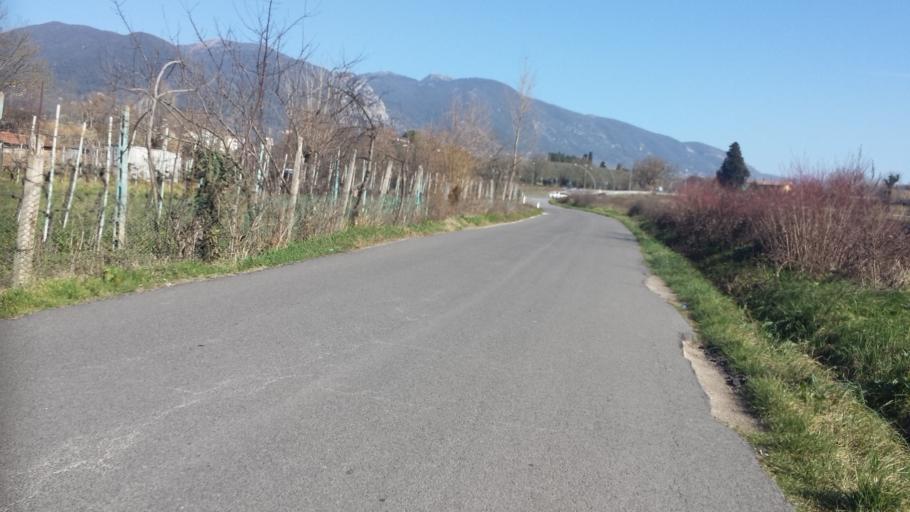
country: IT
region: Umbria
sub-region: Provincia di Terni
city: Terni
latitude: 42.5770
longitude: 12.5924
